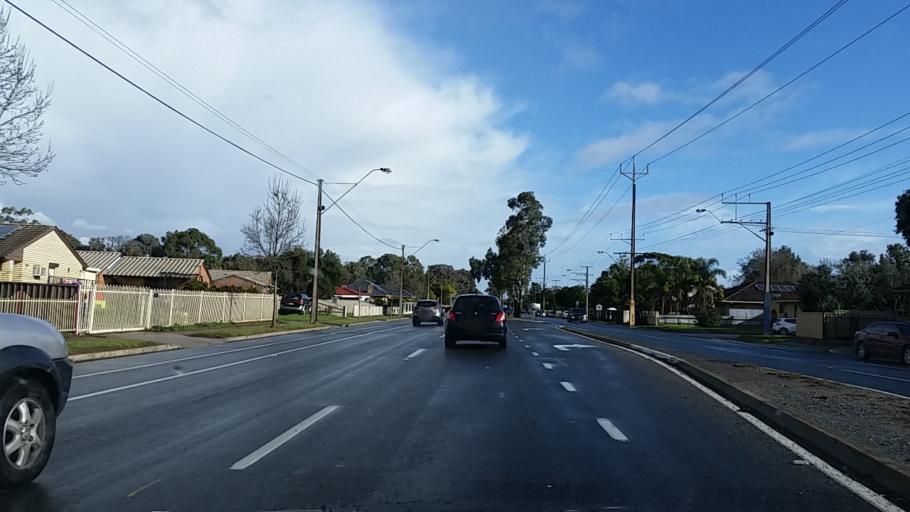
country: AU
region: South Australia
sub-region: Salisbury
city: Salisbury
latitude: -34.7753
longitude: 138.6299
